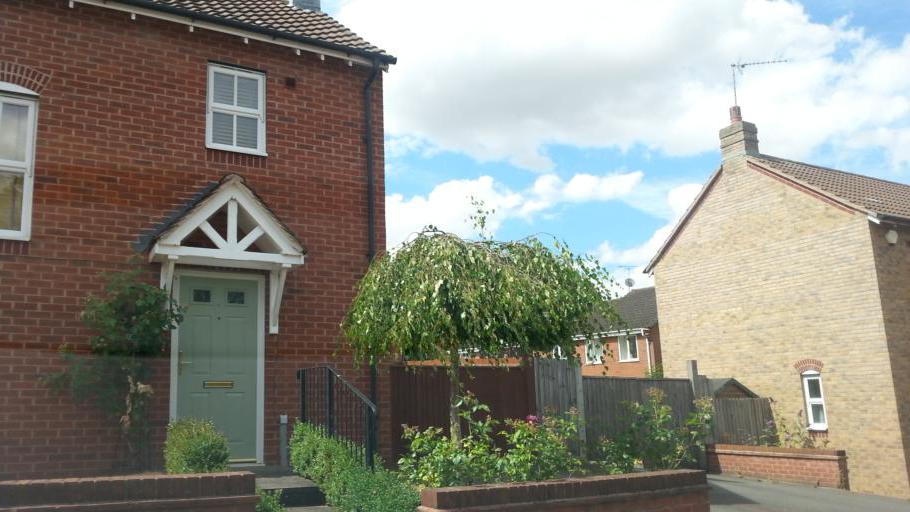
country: GB
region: England
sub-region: Northamptonshire
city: Silverstone
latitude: 52.0891
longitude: -1.0228
